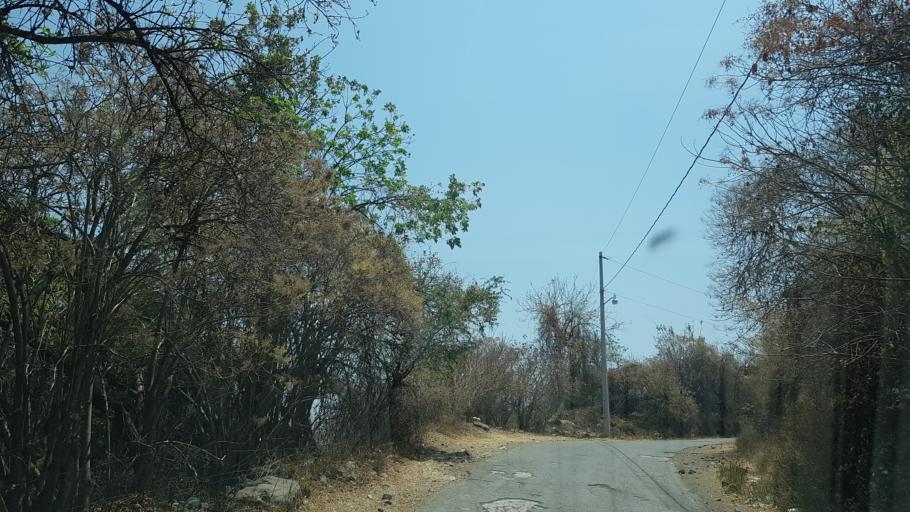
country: MX
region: Puebla
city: Huaquechula
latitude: 18.7798
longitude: -98.5447
